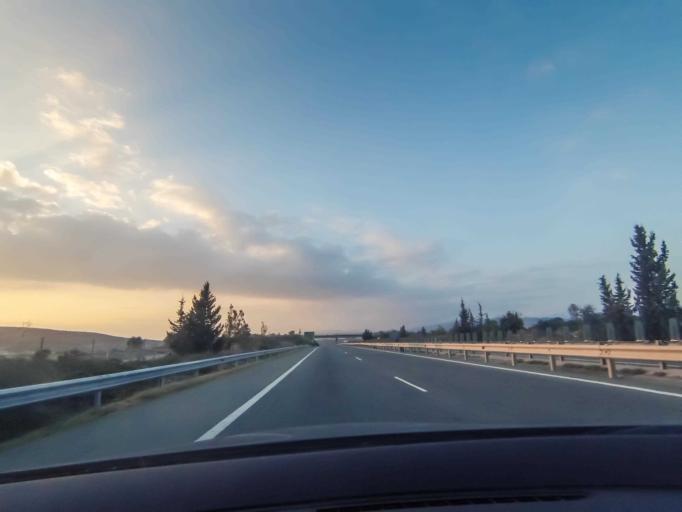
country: CY
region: Limassol
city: Pyrgos
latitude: 34.7271
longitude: 33.2418
